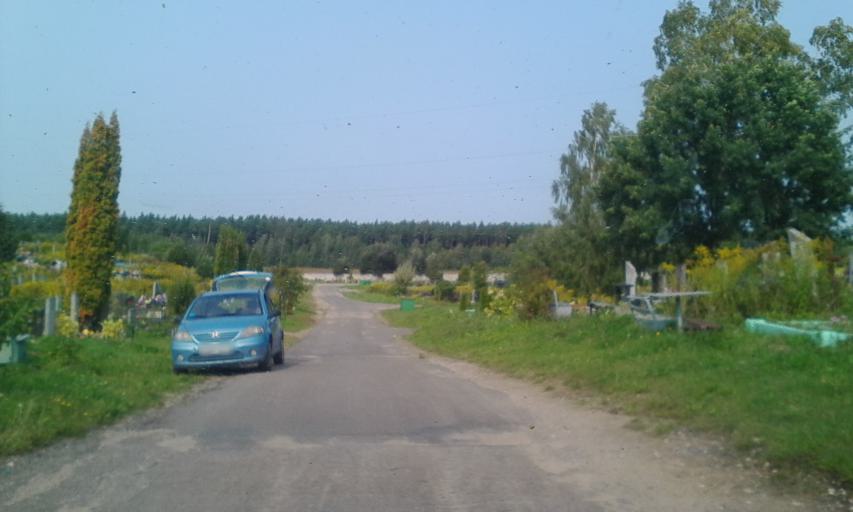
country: BY
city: Michanovichi
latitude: 53.7652
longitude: 27.6972
